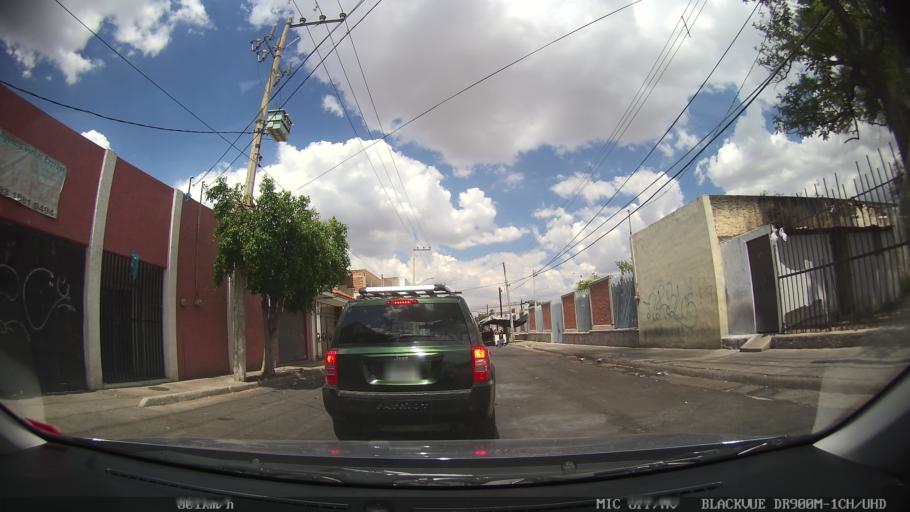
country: MX
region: Jalisco
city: Tlaquepaque
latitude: 20.6591
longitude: -103.2786
